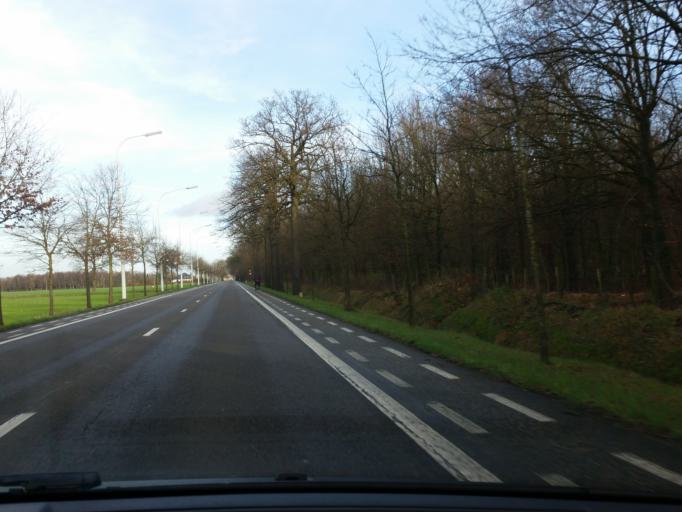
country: BE
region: Flanders
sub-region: Provincie Antwerpen
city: Wuustwezel
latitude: 51.3689
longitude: 4.5659
